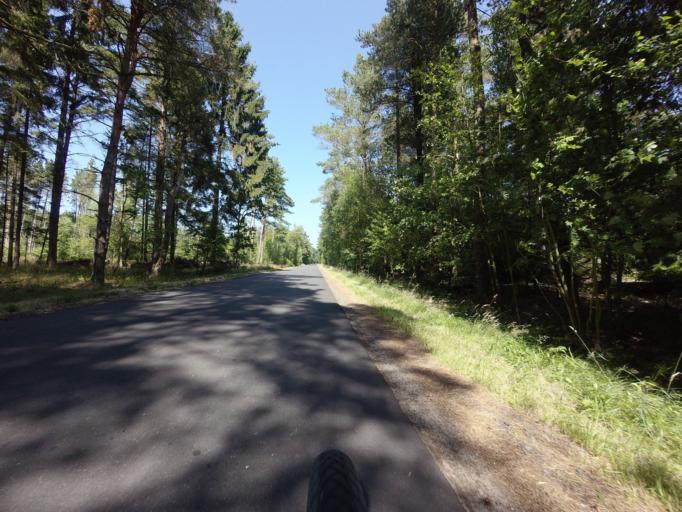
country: DK
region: North Denmark
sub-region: Laeso Kommune
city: Byrum
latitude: 57.2670
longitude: 11.0041
